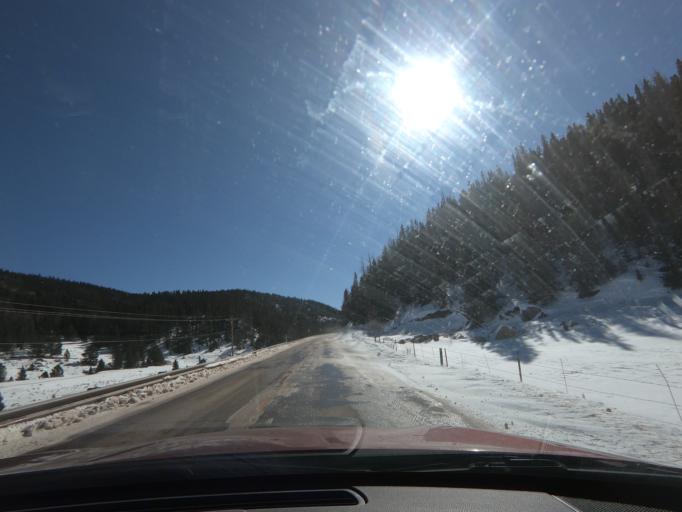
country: US
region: Colorado
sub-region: Teller County
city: Cripple Creek
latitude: 38.7546
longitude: -105.1043
